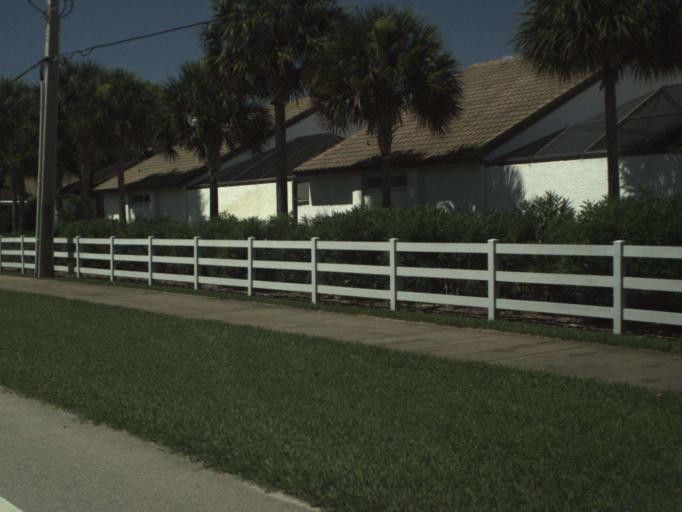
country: US
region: Florida
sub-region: Indian River County
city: South Beach
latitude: 27.5844
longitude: -80.3317
